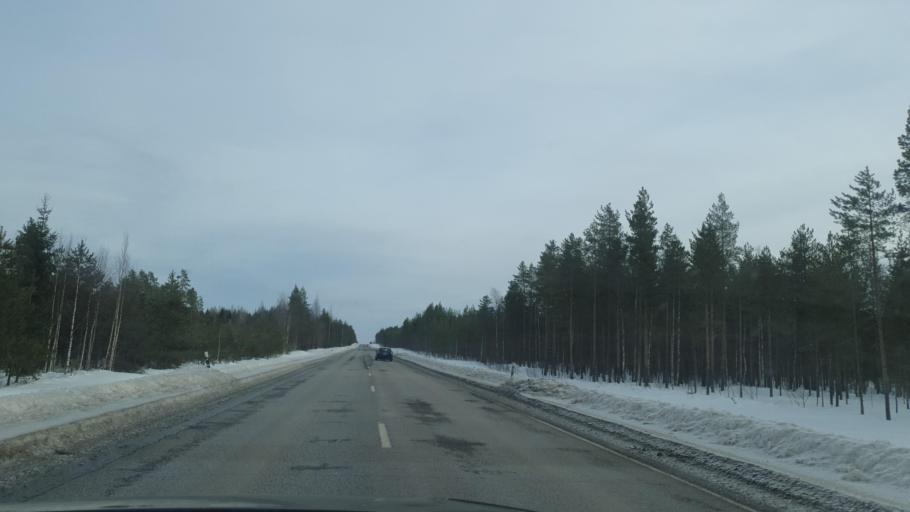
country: FI
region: Kainuu
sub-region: Kajaani
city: Vaala
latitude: 64.5529
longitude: 27.0518
